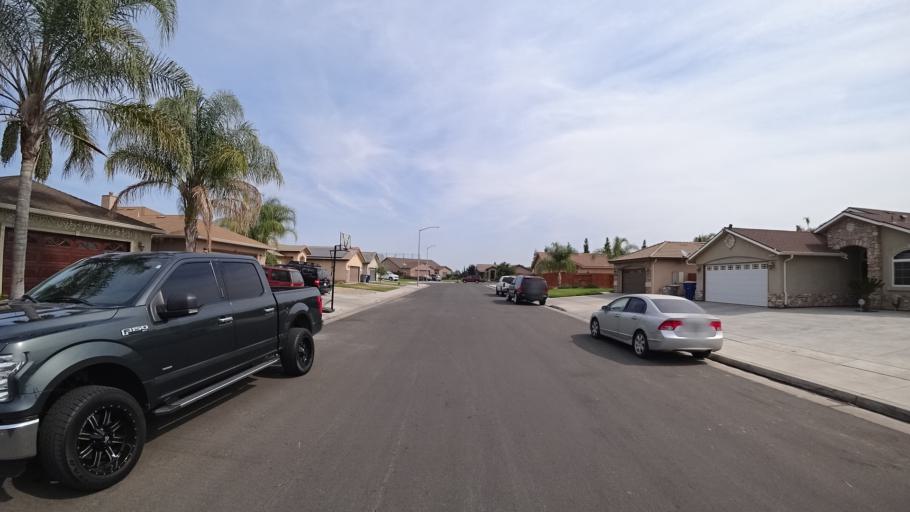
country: US
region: California
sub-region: Fresno County
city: West Park
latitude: 36.7671
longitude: -119.8934
